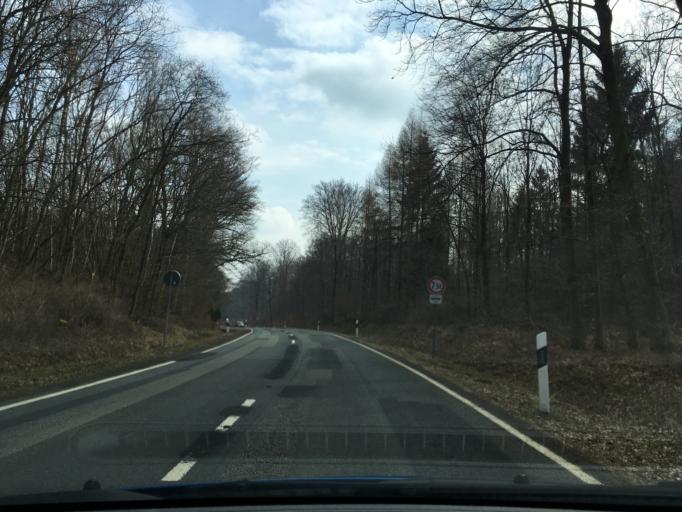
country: DE
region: Lower Saxony
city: Heinade
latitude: 51.7962
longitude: 9.6370
